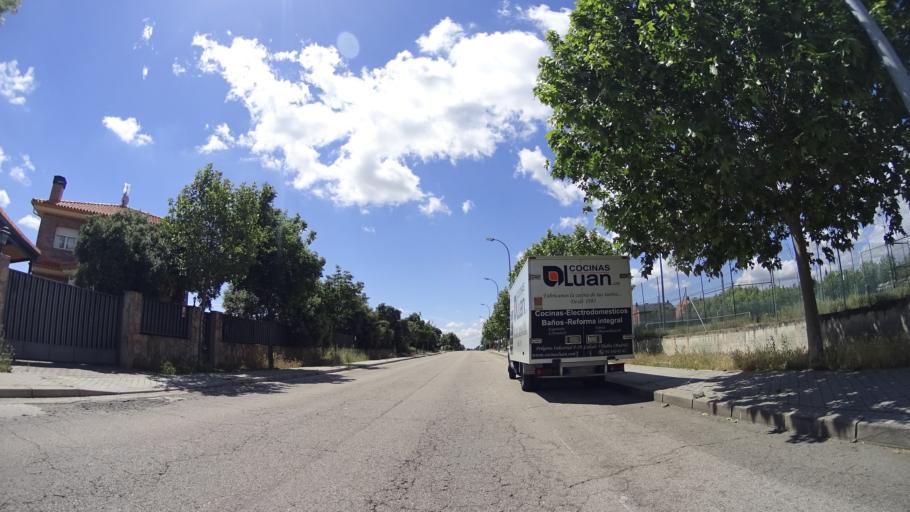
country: ES
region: Madrid
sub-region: Provincia de Madrid
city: Colmenarejo
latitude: 40.5506
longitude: -4.0115
